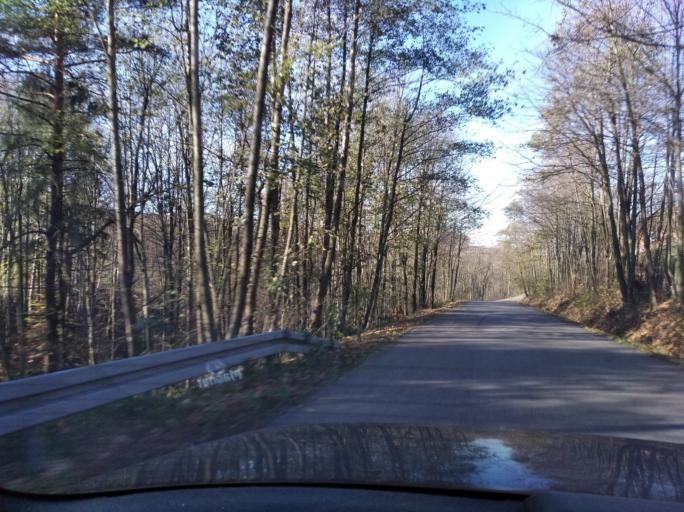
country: PL
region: Subcarpathian Voivodeship
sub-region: Powiat ropczycko-sedziszowski
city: Wielopole Skrzynskie
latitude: 49.9001
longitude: 21.5729
